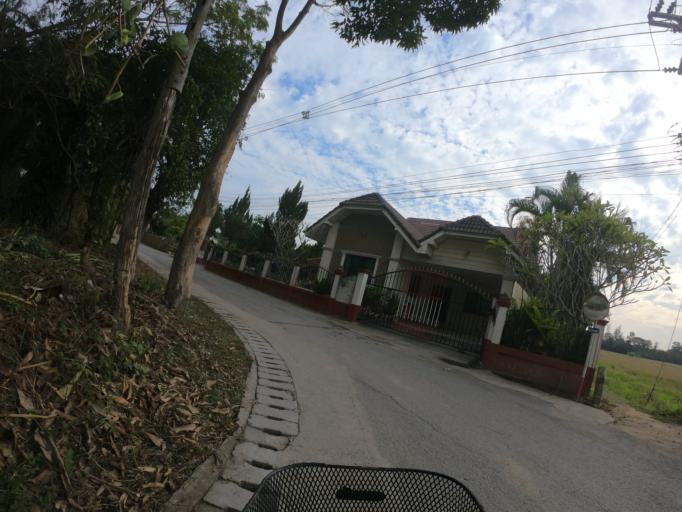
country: TH
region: Chiang Mai
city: San Sai
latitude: 18.7943
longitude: 99.0554
